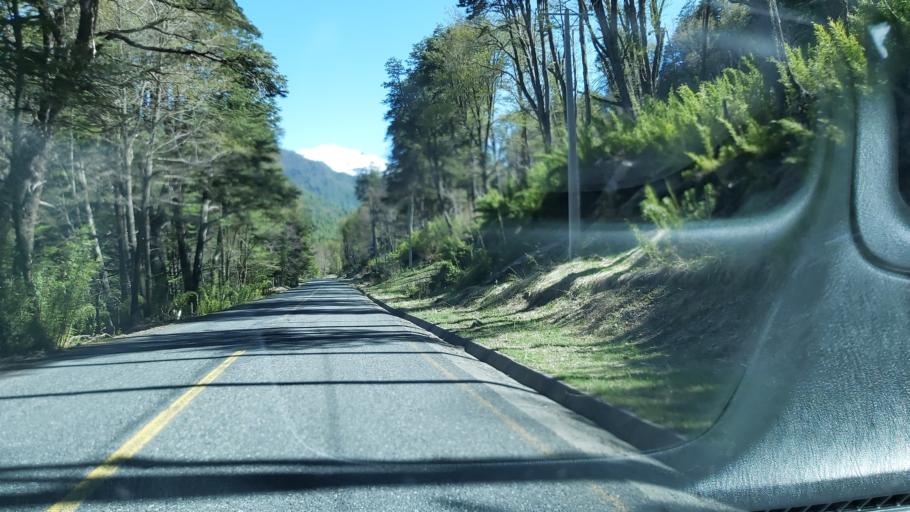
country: CL
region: Araucania
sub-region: Provincia de Cautin
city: Vilcun
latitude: -38.4623
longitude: -71.5171
